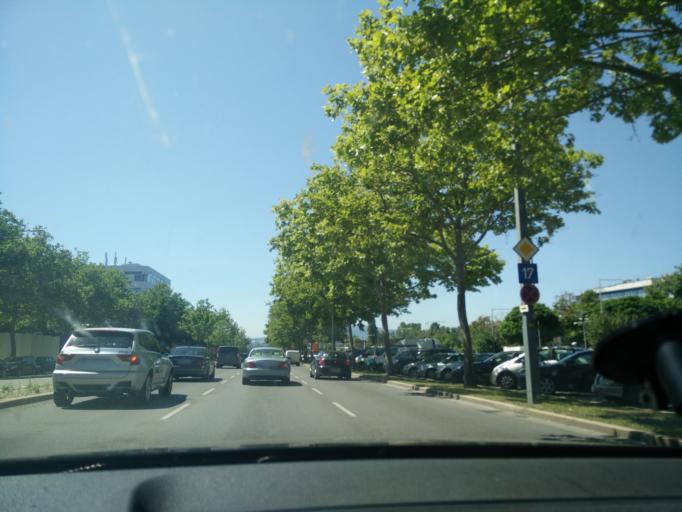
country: AT
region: Vienna
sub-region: Wien Stadt
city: Vienna
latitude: 48.1682
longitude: 16.3489
